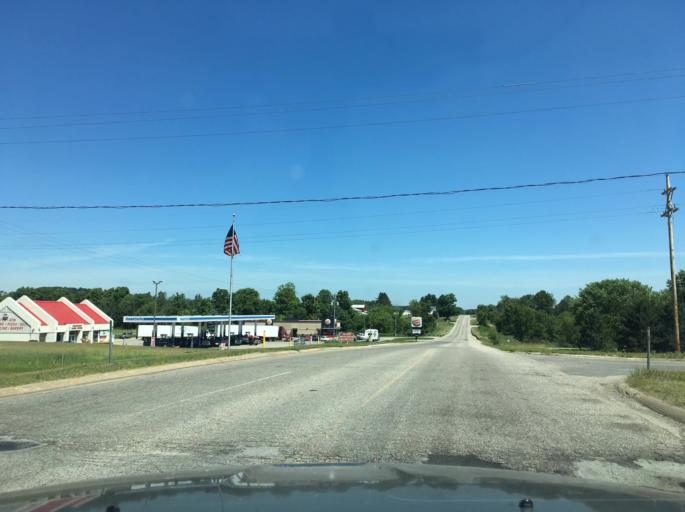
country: US
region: Michigan
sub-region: Osceola County
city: Reed City
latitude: 43.8877
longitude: -85.5229
